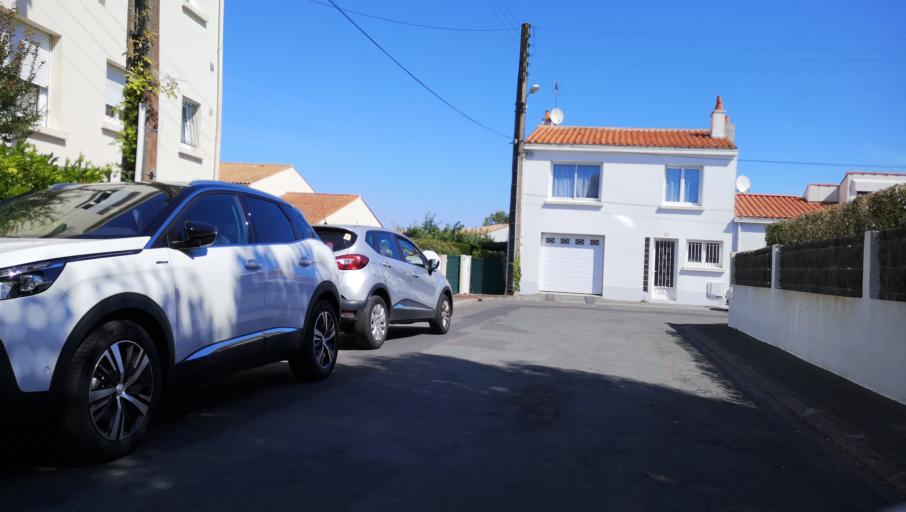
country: FR
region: Pays de la Loire
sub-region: Departement de la Vendee
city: Les Sables-d'Olonne
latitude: 46.4975
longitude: -1.7691
